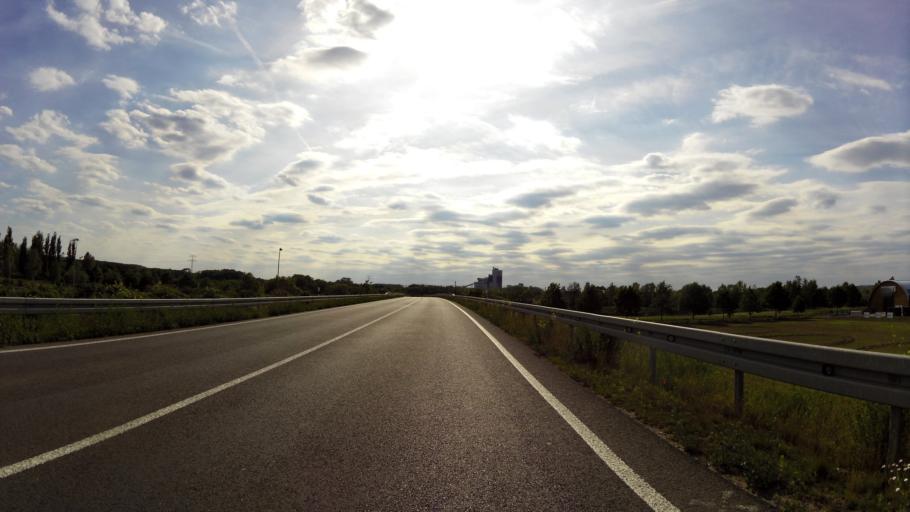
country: DE
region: Brandenburg
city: Rehfelde
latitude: 52.4894
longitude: 13.8650
